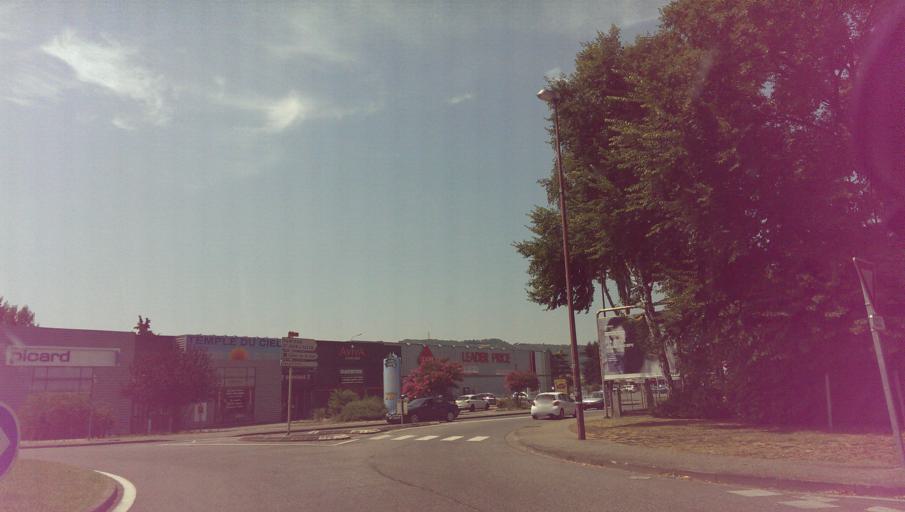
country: FR
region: Midi-Pyrenees
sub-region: Departement de l'Ariege
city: Saint-Jean-du-Falga
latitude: 43.1032
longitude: 1.6293
